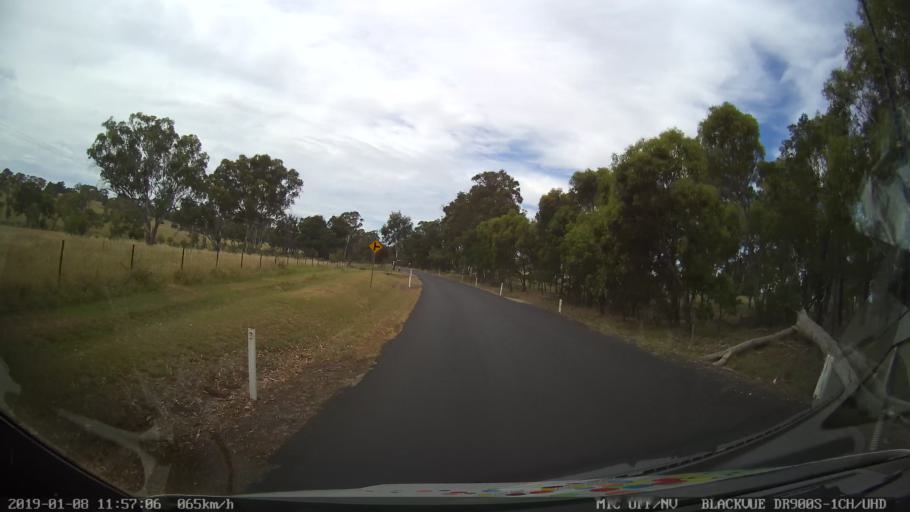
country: AU
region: New South Wales
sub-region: Armidale Dumaresq
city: Armidale
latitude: -30.4471
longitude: 151.5655
